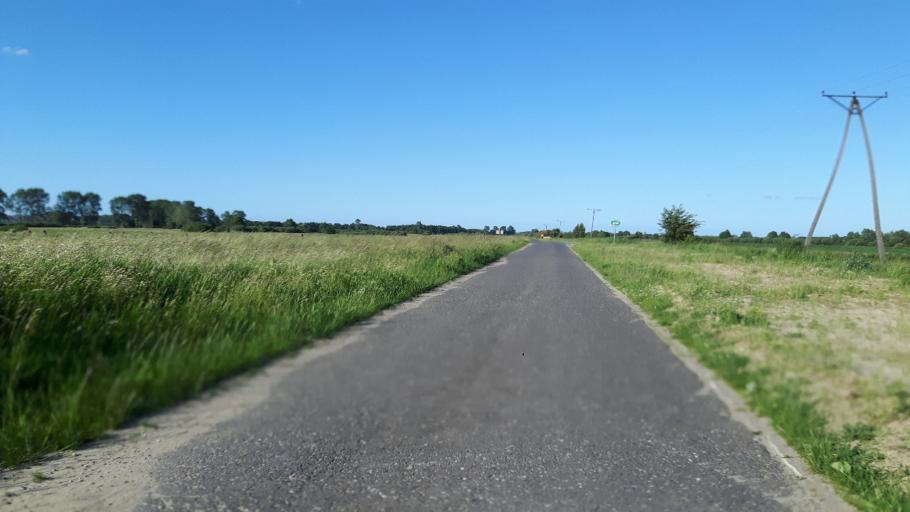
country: PL
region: Pomeranian Voivodeship
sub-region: Powiat wejherowski
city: Rumia
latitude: 54.6082
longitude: 18.4149
